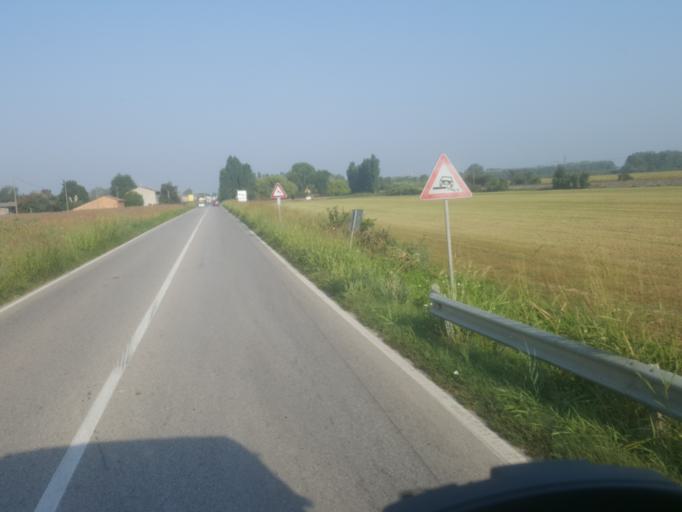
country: IT
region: Emilia-Romagna
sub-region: Provincia di Ravenna
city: Fornace Zarattini
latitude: 44.4500
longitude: 12.1194
